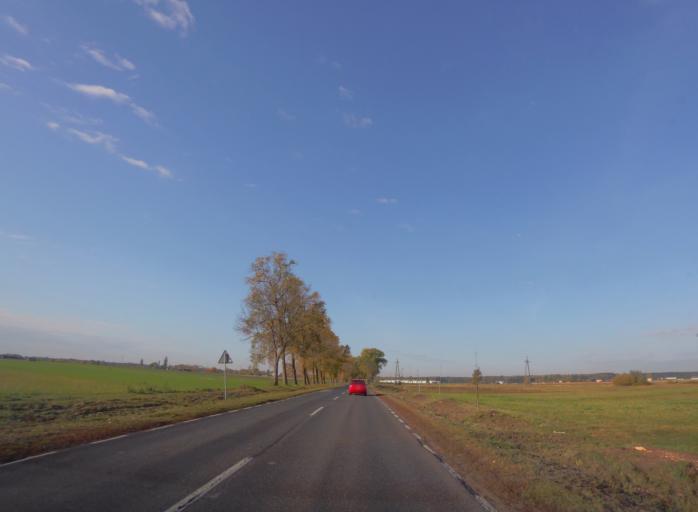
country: PL
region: Masovian Voivodeship
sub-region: Powiat siedlecki
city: Mordy
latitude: 52.2031
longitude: 22.5061
